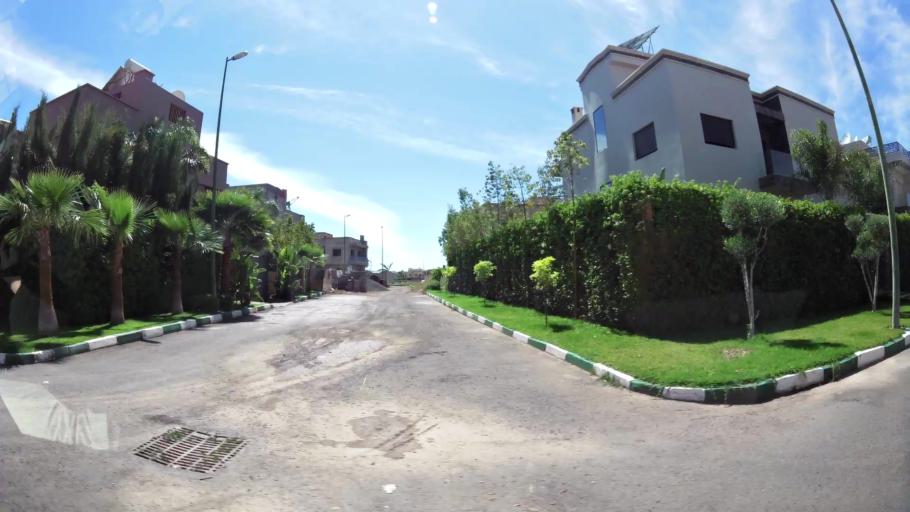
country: MA
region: Marrakech-Tensift-Al Haouz
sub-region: Marrakech
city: Marrakesh
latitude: 31.6533
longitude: -8.0730
